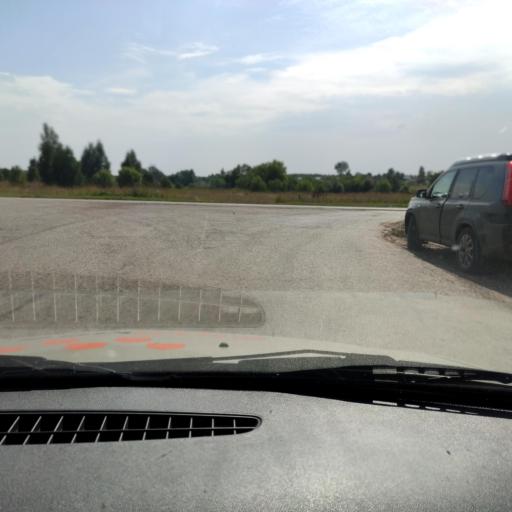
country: RU
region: Bashkortostan
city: Pavlovka
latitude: 55.3913
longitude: 56.4643
